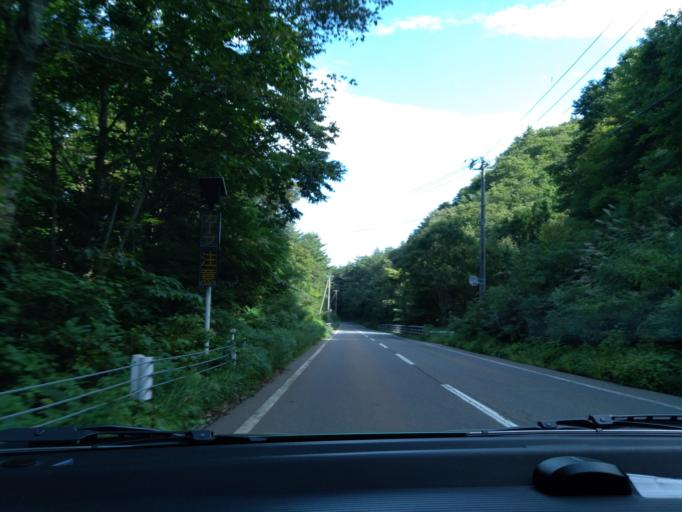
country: JP
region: Iwate
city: Shizukuishi
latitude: 39.6270
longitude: 141.0638
